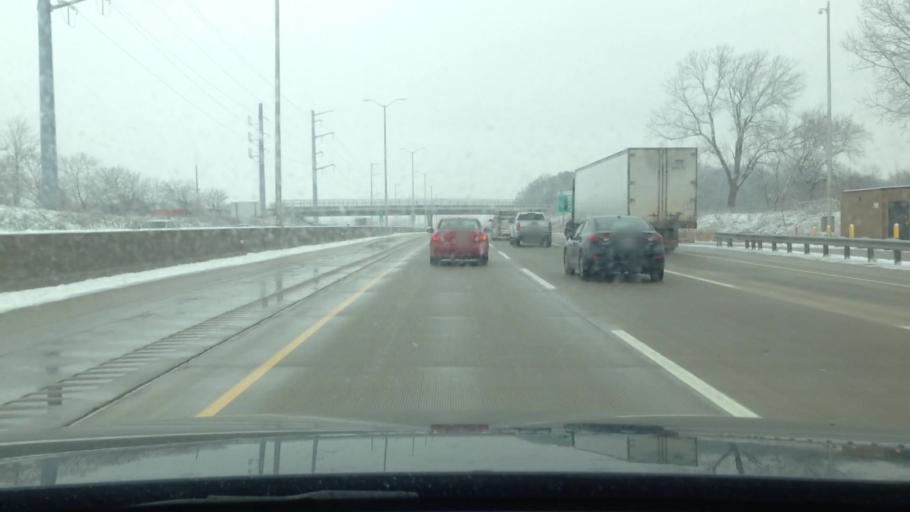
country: US
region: Illinois
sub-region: Kane County
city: Gilberts
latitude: 42.1092
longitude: -88.4056
